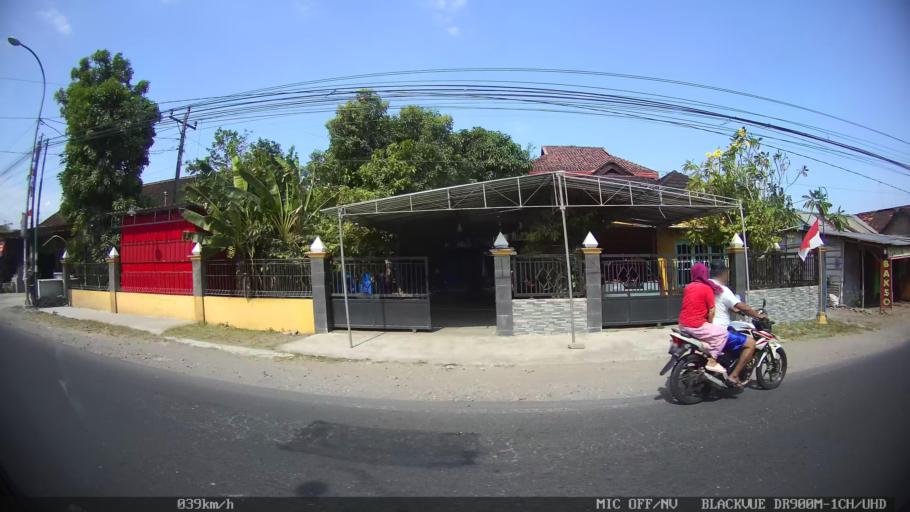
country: ID
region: Daerah Istimewa Yogyakarta
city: Sewon
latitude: -7.8957
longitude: 110.3850
